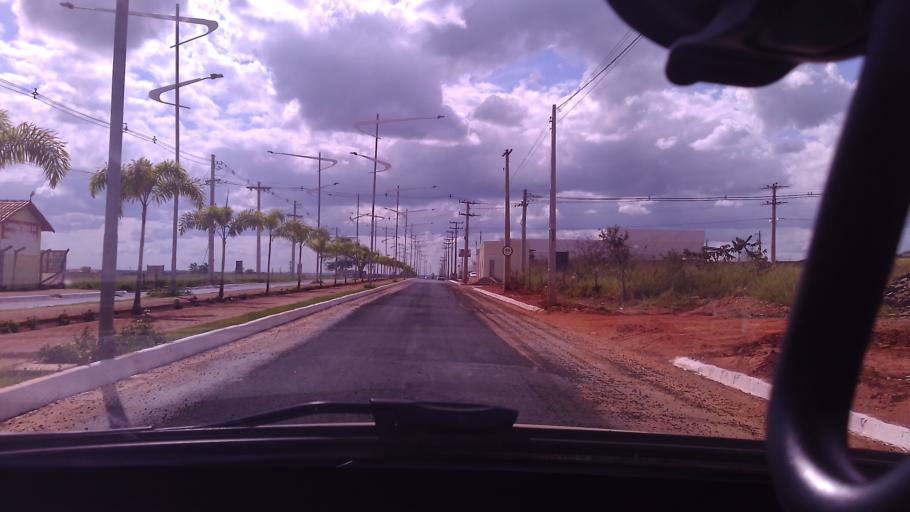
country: BR
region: Goias
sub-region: Mineiros
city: Mineiros
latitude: -17.5407
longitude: -52.5394
